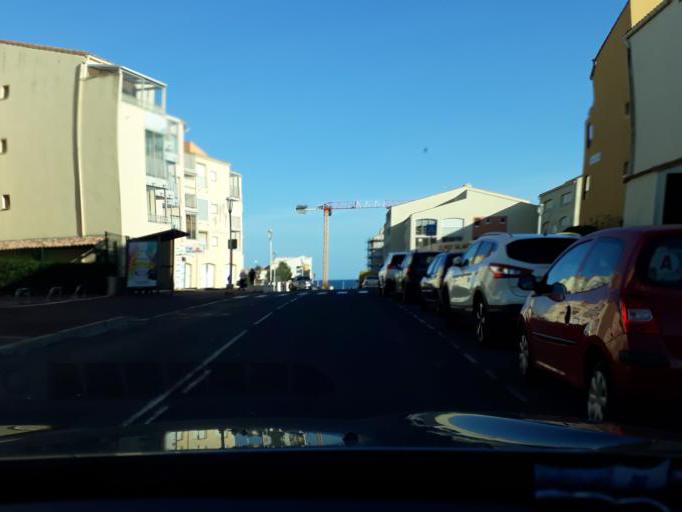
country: FR
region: Languedoc-Roussillon
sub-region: Departement de l'Herault
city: Le Cap d'Agde
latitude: 43.2818
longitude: 3.5172
